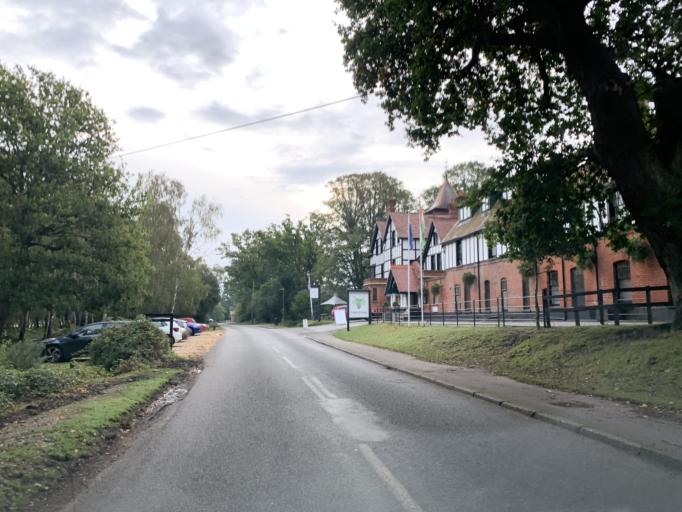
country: GB
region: England
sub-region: Hampshire
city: Brockenhurst
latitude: 50.8227
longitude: -1.5863
